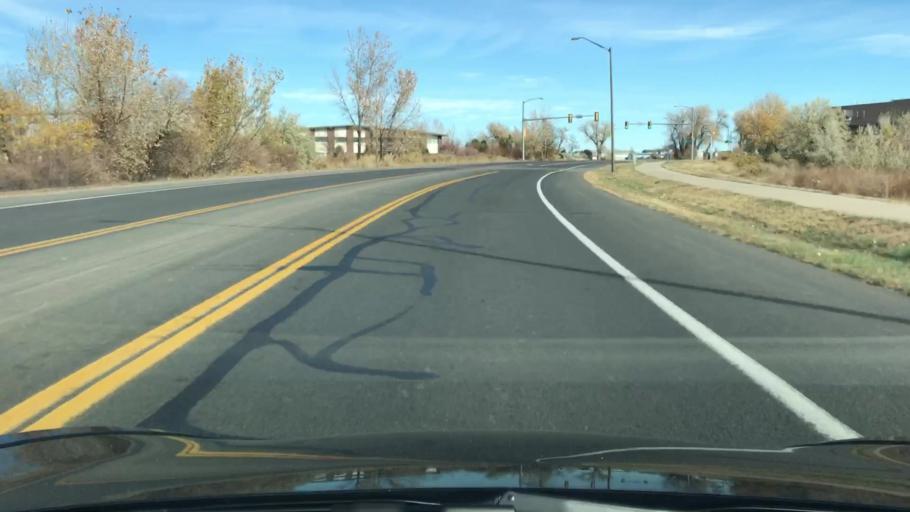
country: US
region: Colorado
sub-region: Larimer County
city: Fort Collins
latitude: 40.5845
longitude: -105.0324
